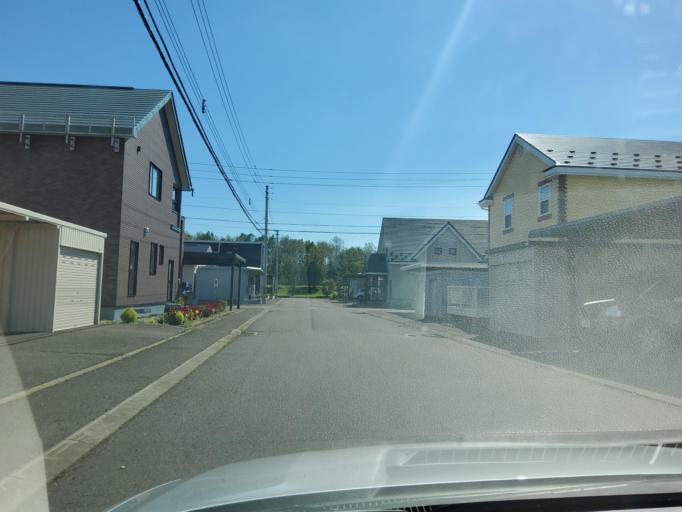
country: JP
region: Hokkaido
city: Obihiro
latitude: 42.9403
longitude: 143.2200
